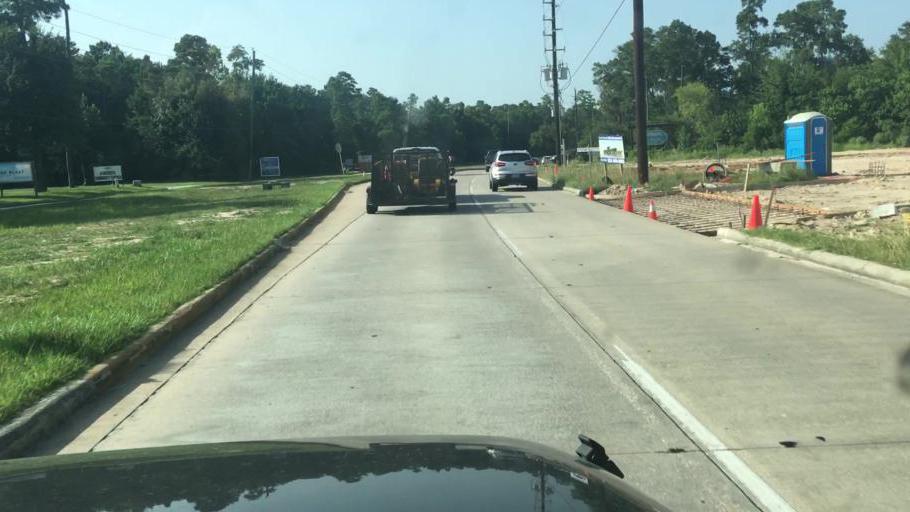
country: US
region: Texas
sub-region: Harris County
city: Atascocita
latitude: 29.9724
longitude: -95.1716
